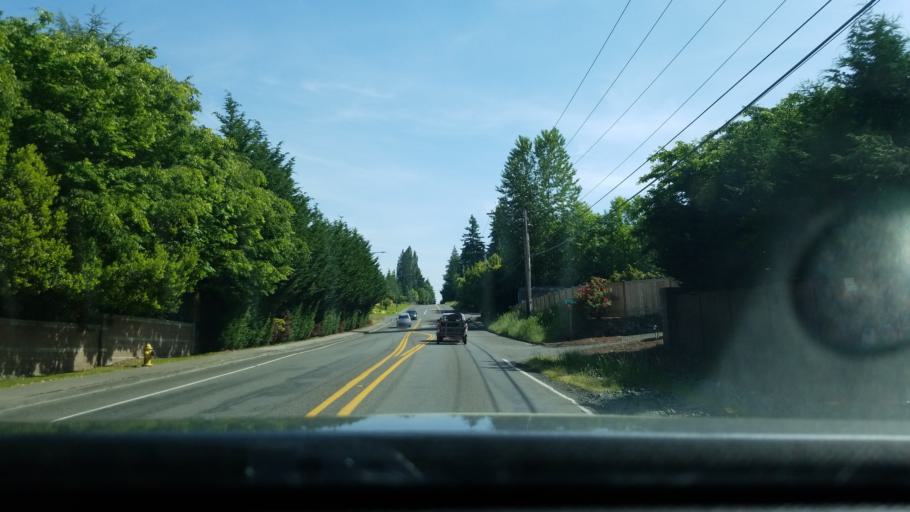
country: US
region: Washington
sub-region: Pierce County
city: Puyallup
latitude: 47.1693
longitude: -122.3043
